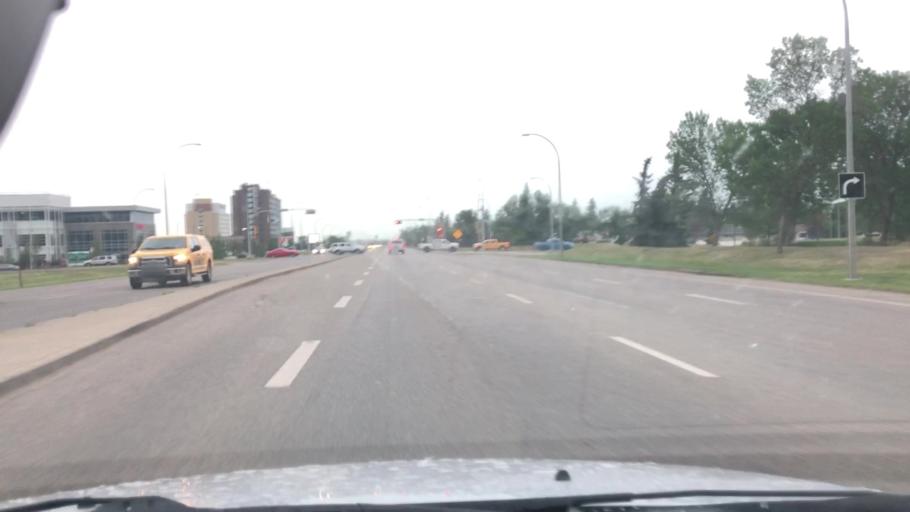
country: CA
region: Alberta
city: St. Albert
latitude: 53.5509
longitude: -113.6092
